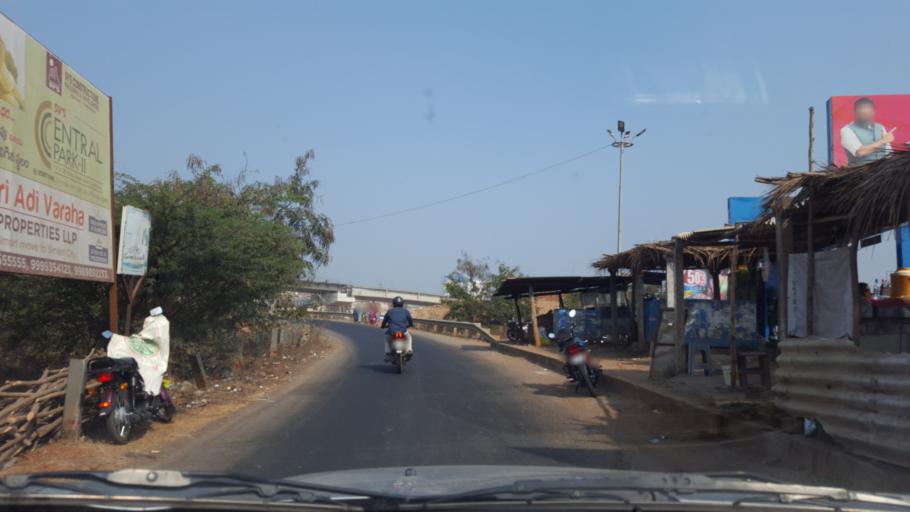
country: IN
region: Andhra Pradesh
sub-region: Vishakhapatnam
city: Bhimunipatnam
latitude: 17.8932
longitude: 83.3779
